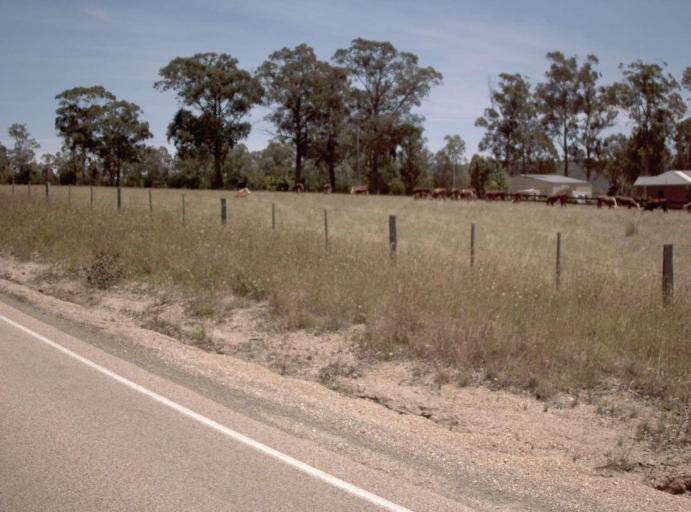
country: AU
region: Victoria
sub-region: East Gippsland
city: Lakes Entrance
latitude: -37.6830
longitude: 147.8448
